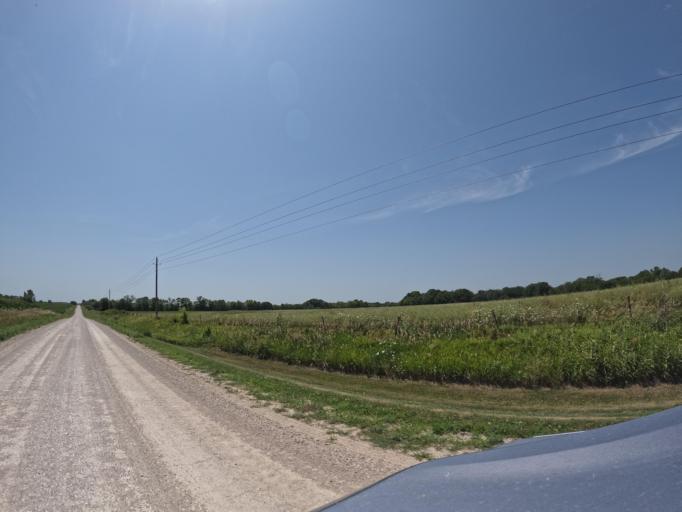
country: US
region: Iowa
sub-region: Henry County
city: Mount Pleasant
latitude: 40.9221
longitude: -91.6458
